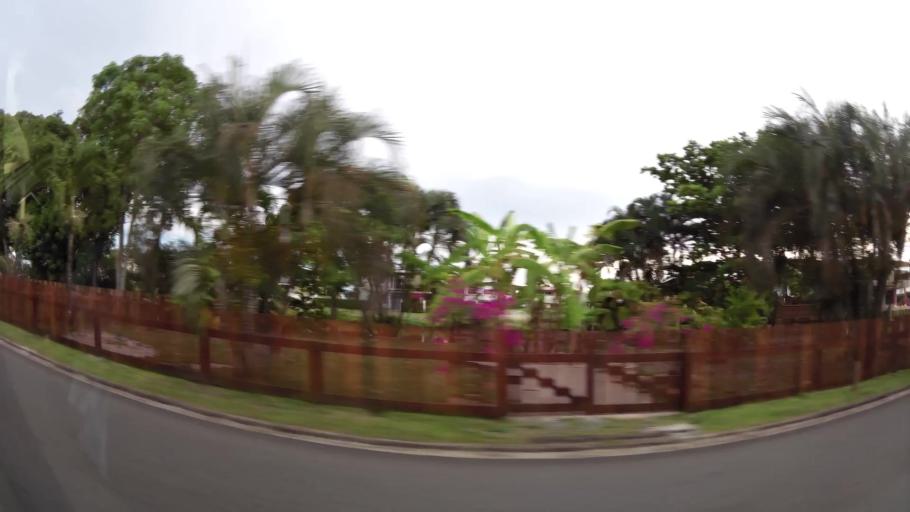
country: SR
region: Paramaribo
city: Paramaribo
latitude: 5.8467
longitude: -55.1393
